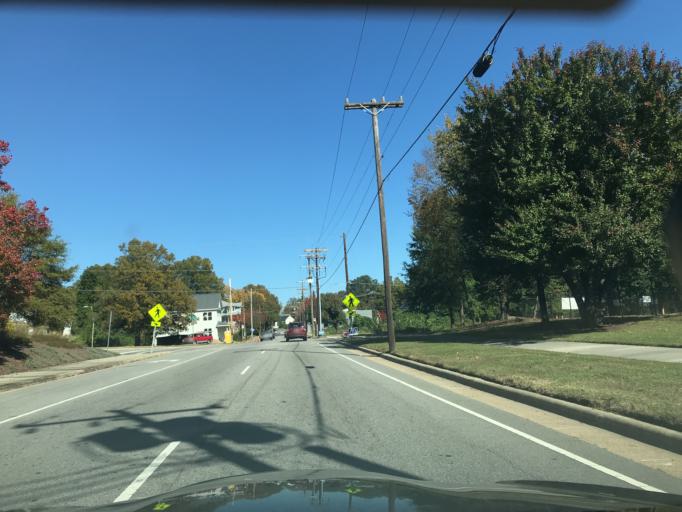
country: US
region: North Carolina
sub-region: Durham County
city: Durham
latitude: 35.9966
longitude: -78.8960
